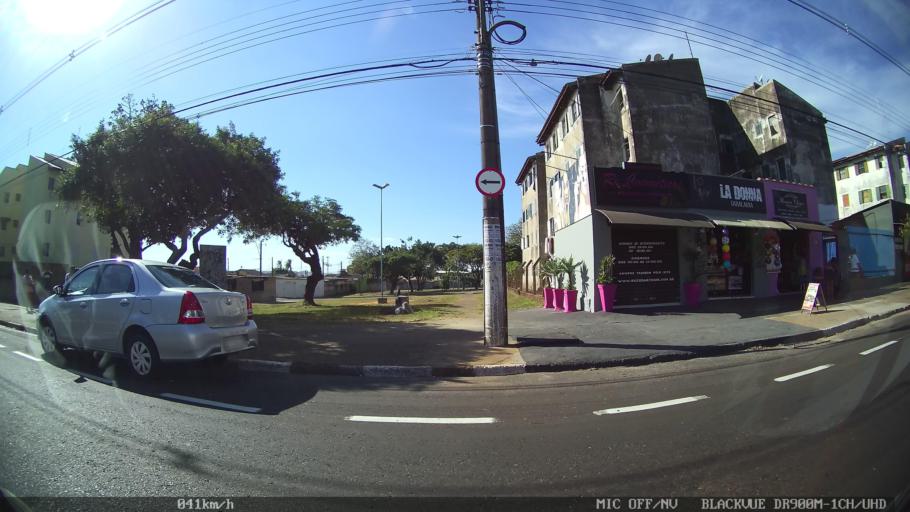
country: BR
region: Sao Paulo
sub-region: Franca
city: Franca
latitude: -20.5012
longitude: -47.4115
